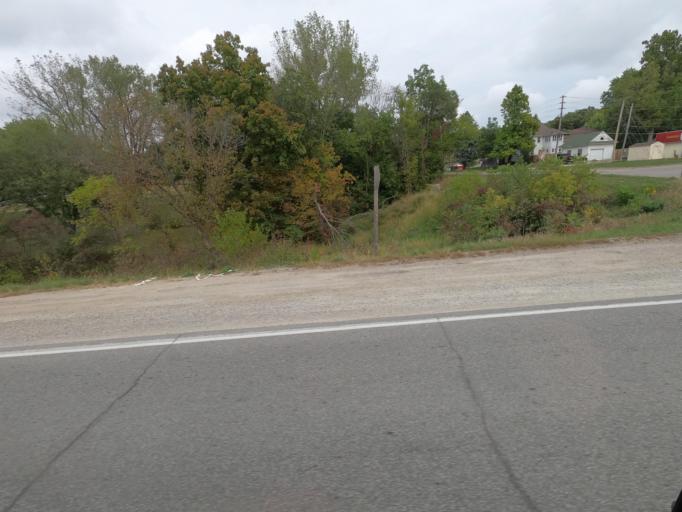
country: US
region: Iowa
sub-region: Wapello County
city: Ottumwa
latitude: 40.9218
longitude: -92.2286
